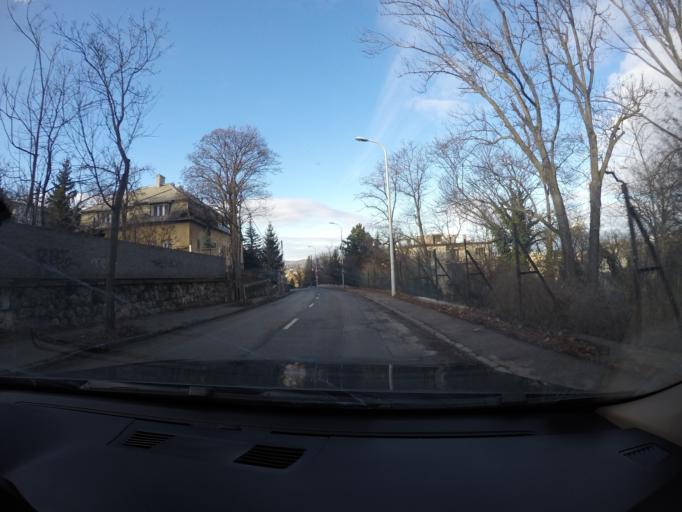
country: HU
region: Budapest
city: Budapest I. keruelet
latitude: 47.4868
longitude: 19.0395
